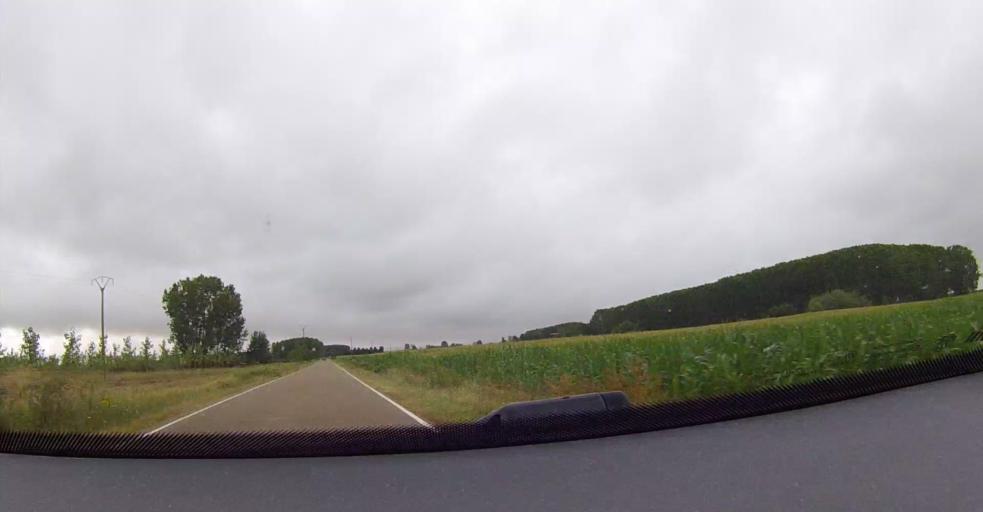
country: ES
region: Castille and Leon
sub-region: Provincia de Palencia
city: Pedrosa de la Vega
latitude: 42.4819
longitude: -4.7271
